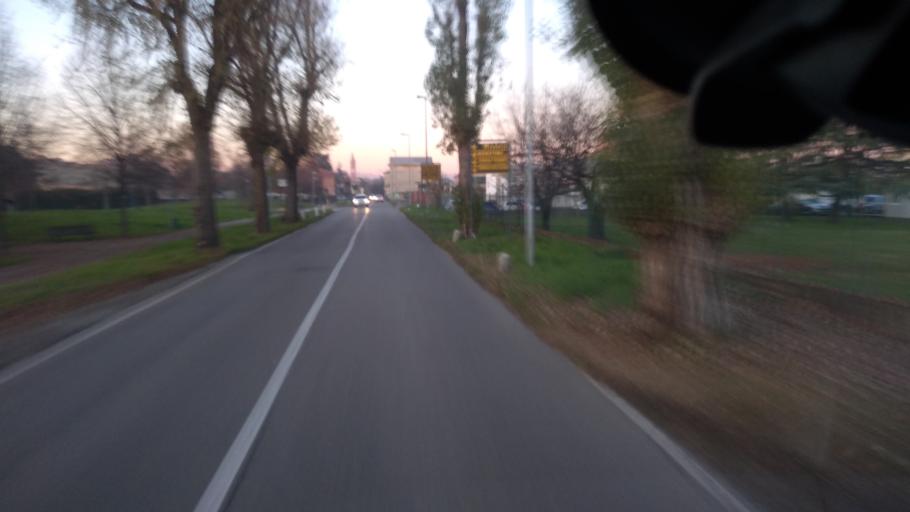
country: IT
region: Lombardy
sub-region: Provincia di Bergamo
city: Treviglio
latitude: 45.5122
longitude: 9.5943
